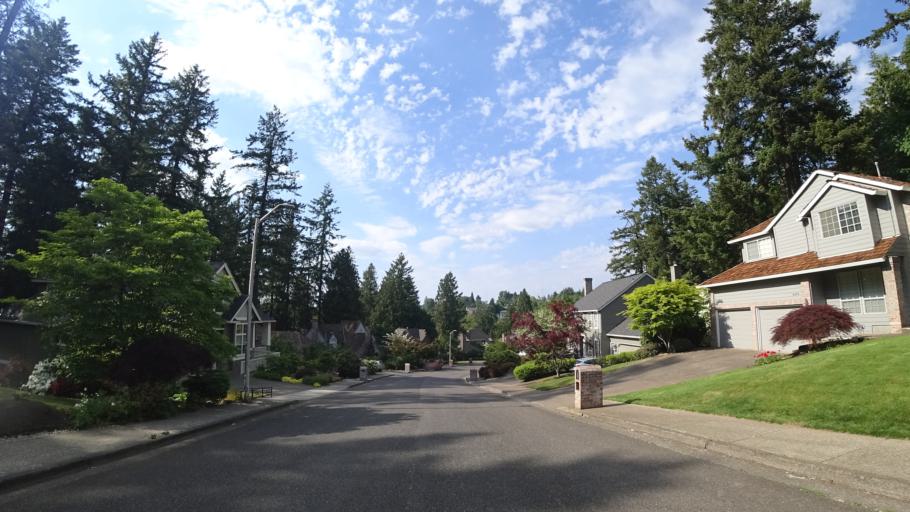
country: US
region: Oregon
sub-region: Washington County
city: Garden Home-Whitford
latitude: 45.4597
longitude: -122.7407
